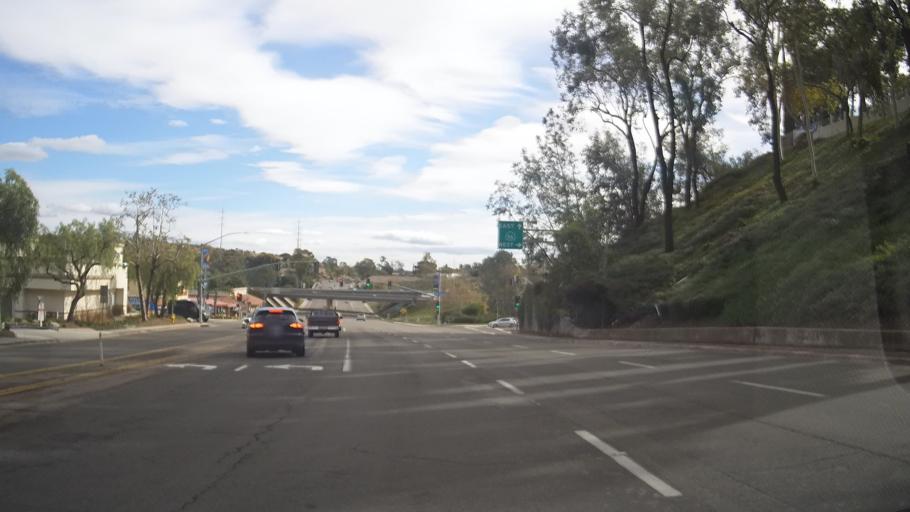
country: US
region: California
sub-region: San Diego County
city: Fairbanks Ranch
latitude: 32.9600
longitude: -117.1166
